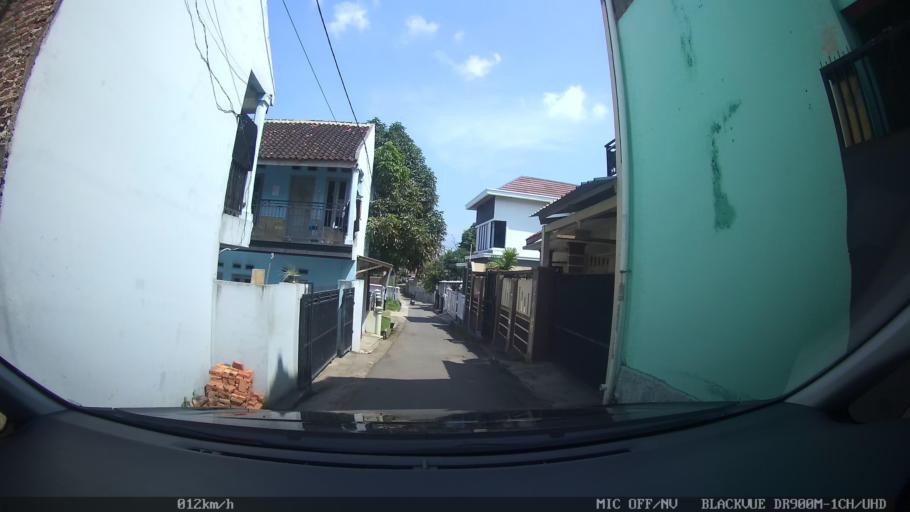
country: ID
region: Lampung
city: Kedaton
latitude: -5.3682
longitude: 105.2497
